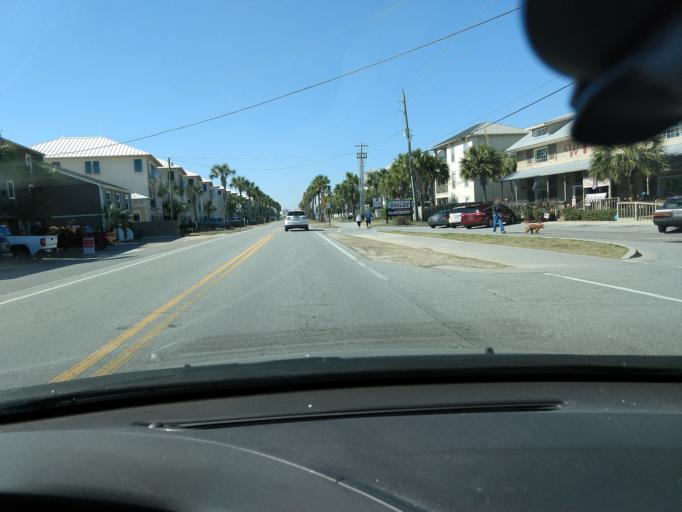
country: US
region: Florida
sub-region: Walton County
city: Miramar Beach
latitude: 30.3769
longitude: -86.3764
